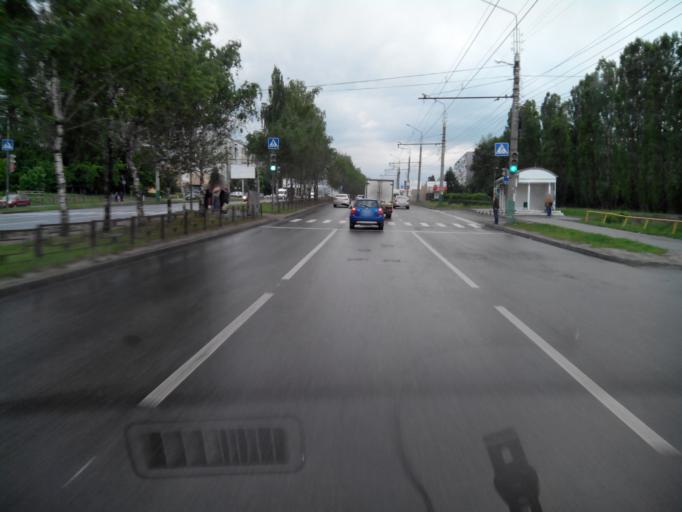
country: RU
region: Penza
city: Bogoslovka
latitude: 53.2222
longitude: 44.9026
